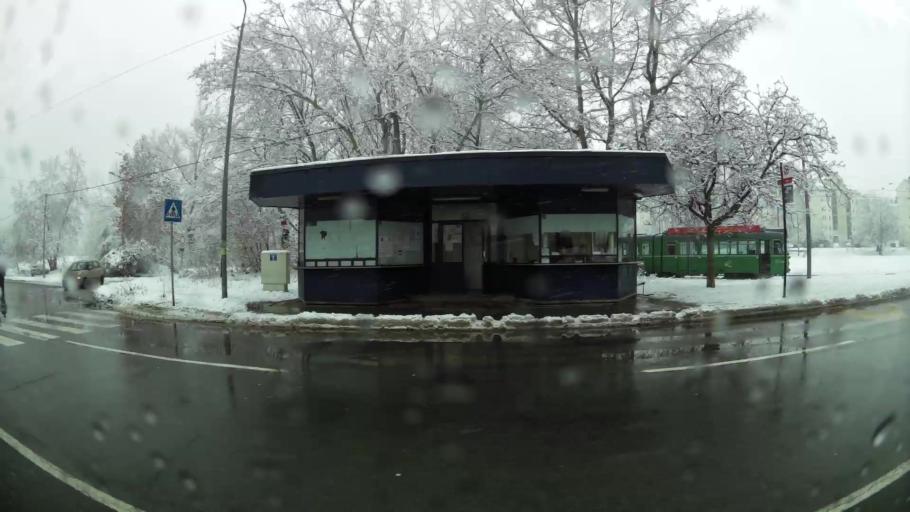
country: RS
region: Central Serbia
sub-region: Belgrade
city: Cukarica
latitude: 44.7928
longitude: 20.3753
